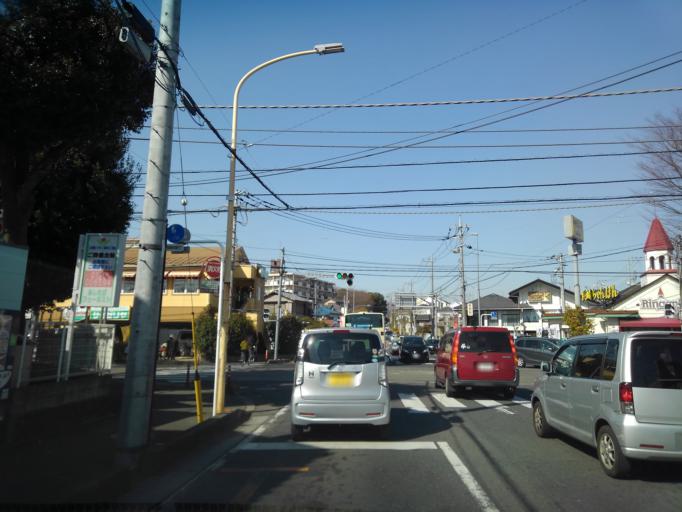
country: JP
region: Saitama
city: Tokorozawa
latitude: 35.7962
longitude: 139.4808
